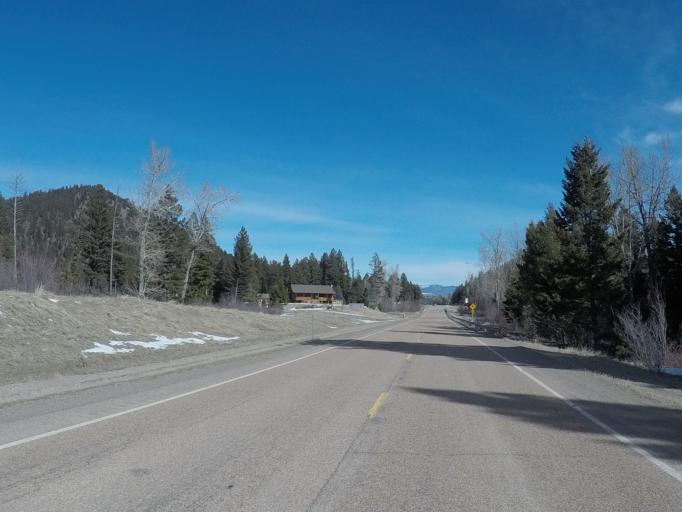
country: US
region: Montana
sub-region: Granite County
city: Philipsburg
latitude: 46.4675
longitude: -113.2347
